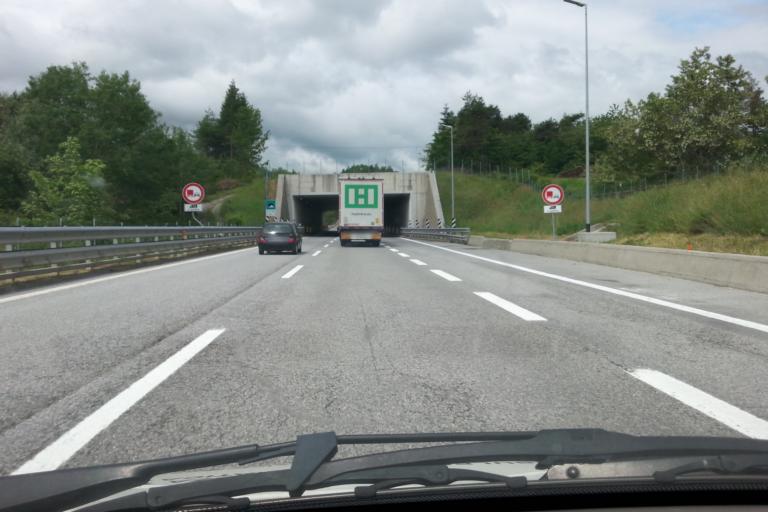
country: IT
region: Liguria
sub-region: Provincia di Savona
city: Roccavignale
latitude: 44.3563
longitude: 8.1964
